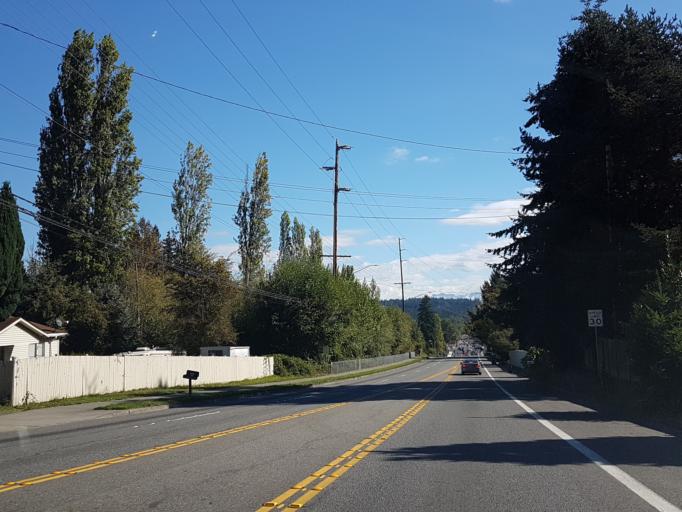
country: US
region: Washington
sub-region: King County
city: Bothell
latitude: 47.7912
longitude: -122.2256
